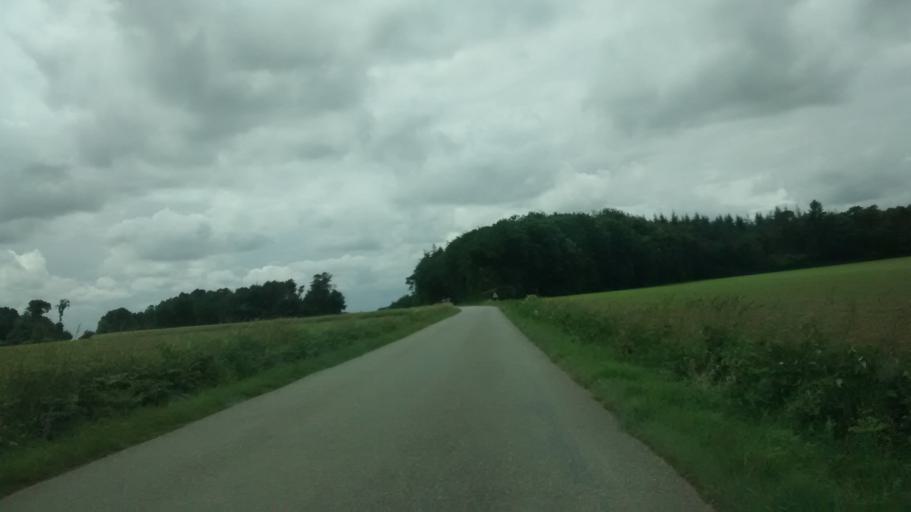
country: FR
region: Brittany
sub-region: Departement du Morbihan
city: Carentoir
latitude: 47.8269
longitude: -2.1730
